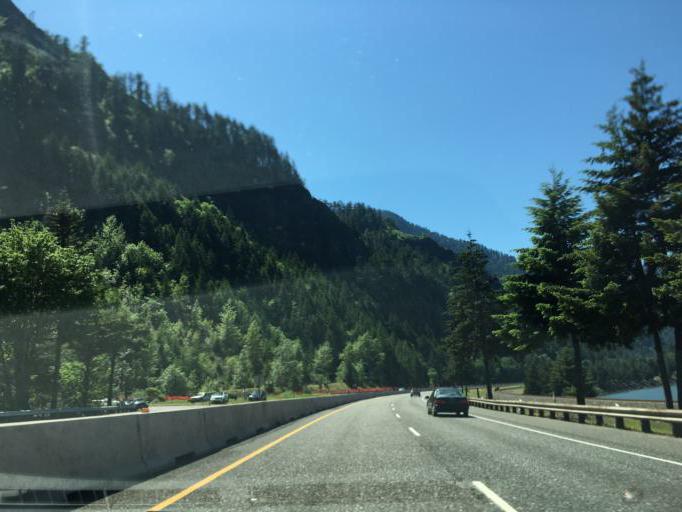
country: US
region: Washington
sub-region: Skamania County
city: Carson
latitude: 45.6894
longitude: -121.6901
